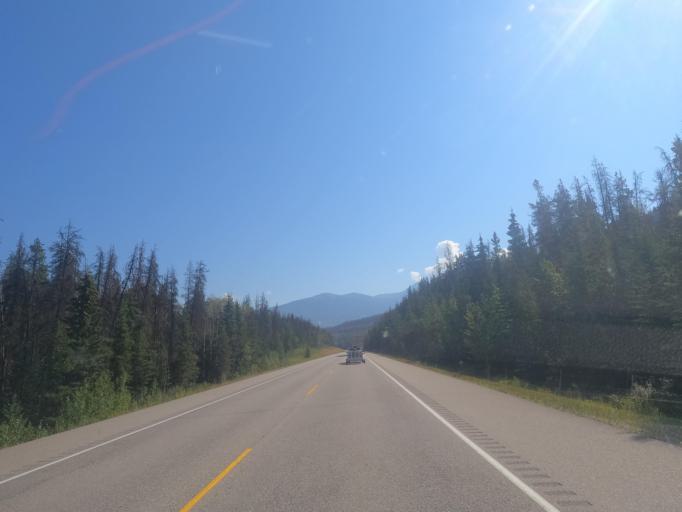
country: CA
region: Alberta
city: Jasper Park Lodge
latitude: 52.8574
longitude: -118.1303
